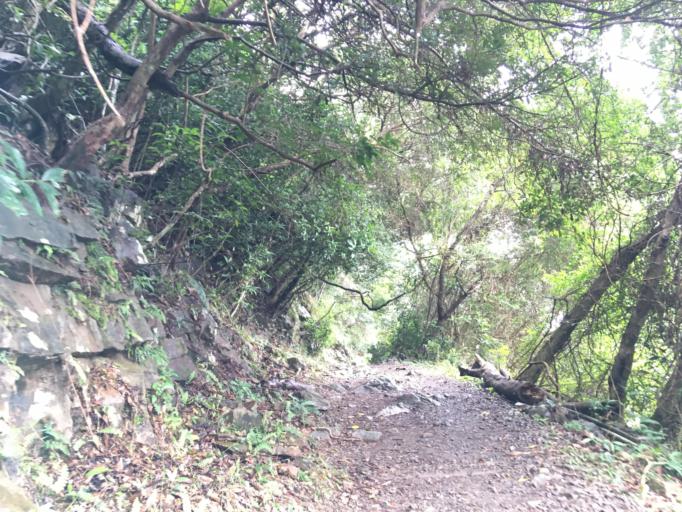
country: TW
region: Taiwan
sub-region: Yilan
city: Yilan
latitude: 24.8381
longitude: 121.7750
